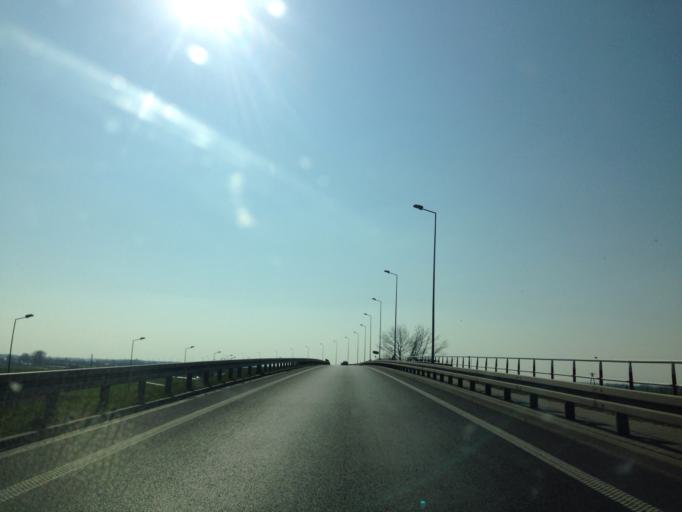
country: PL
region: Lower Silesian Voivodeship
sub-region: Powiat olesnicki
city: Olesnica
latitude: 51.2131
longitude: 17.3498
